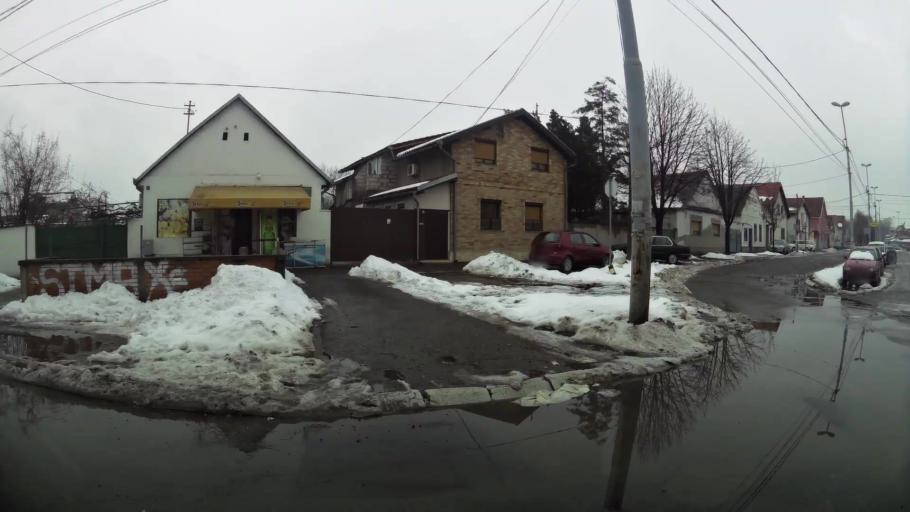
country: RS
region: Central Serbia
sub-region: Belgrade
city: Zemun
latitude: 44.8480
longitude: 20.3793
